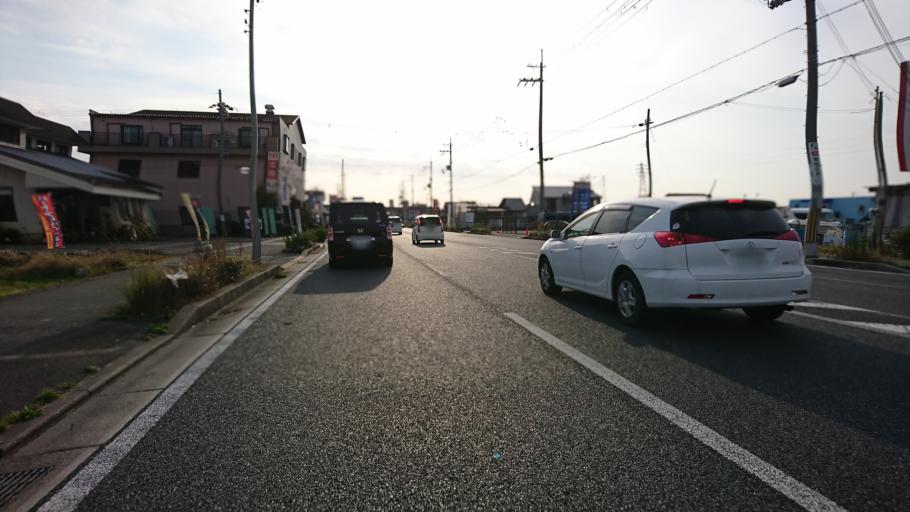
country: JP
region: Hyogo
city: Kakogawacho-honmachi
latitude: 34.7120
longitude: 134.8840
